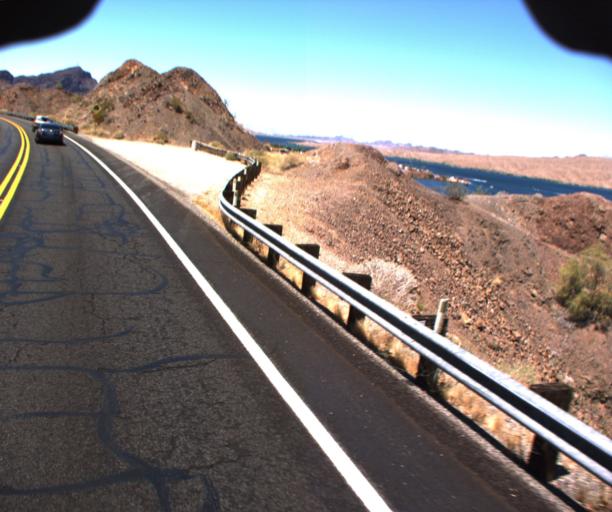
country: US
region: Arizona
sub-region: La Paz County
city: Cienega Springs
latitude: 34.2910
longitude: -114.1155
